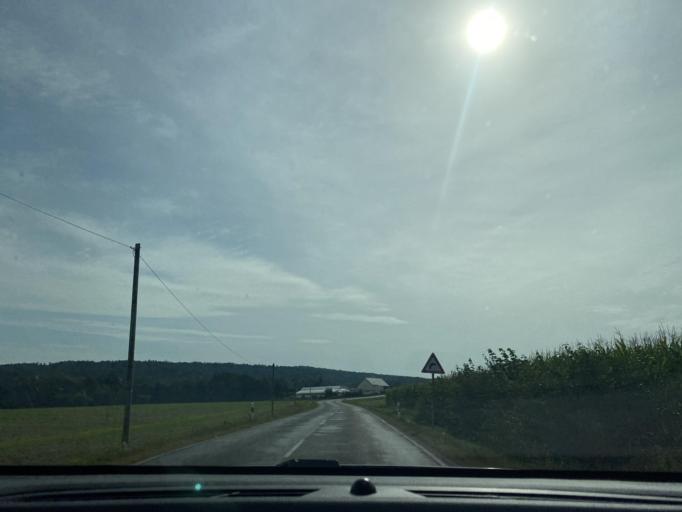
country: DE
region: Saxony
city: Reichenbach
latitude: 51.1871
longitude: 14.7620
